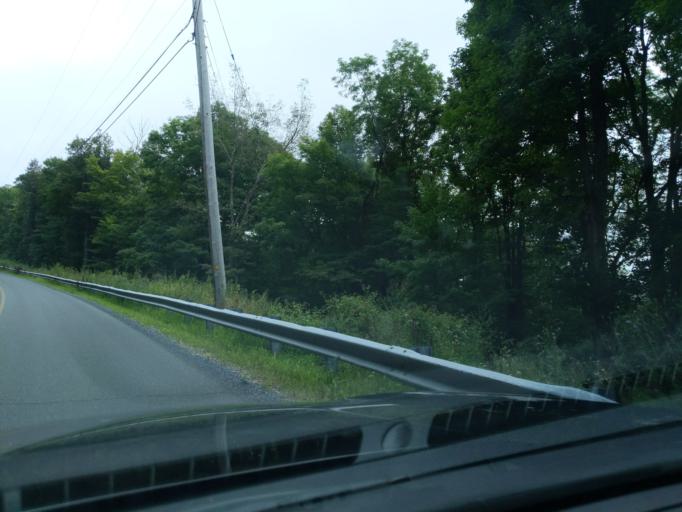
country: US
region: Pennsylvania
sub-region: Cambria County
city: Beaverdale
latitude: 40.2930
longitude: -78.5780
